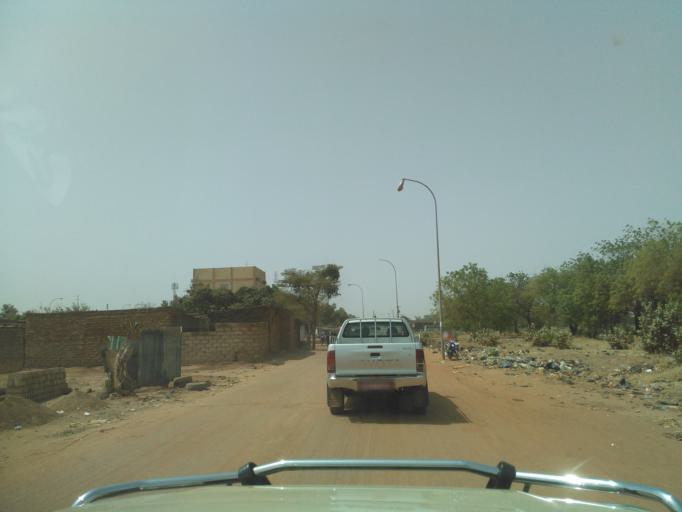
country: BF
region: Centre
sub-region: Kadiogo Province
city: Ouagadougou
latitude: 12.3969
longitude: -1.5534
